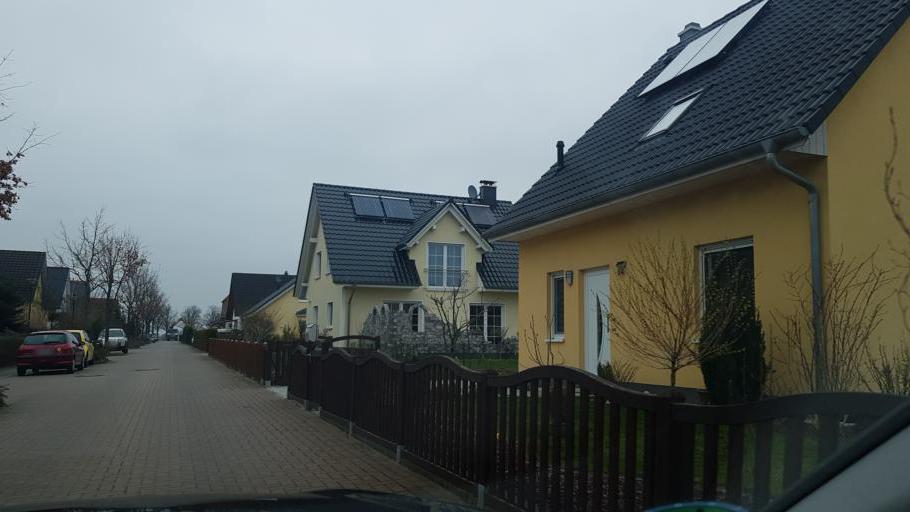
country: DE
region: Brandenburg
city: Mittenwalde
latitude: 52.2898
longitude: 13.5357
